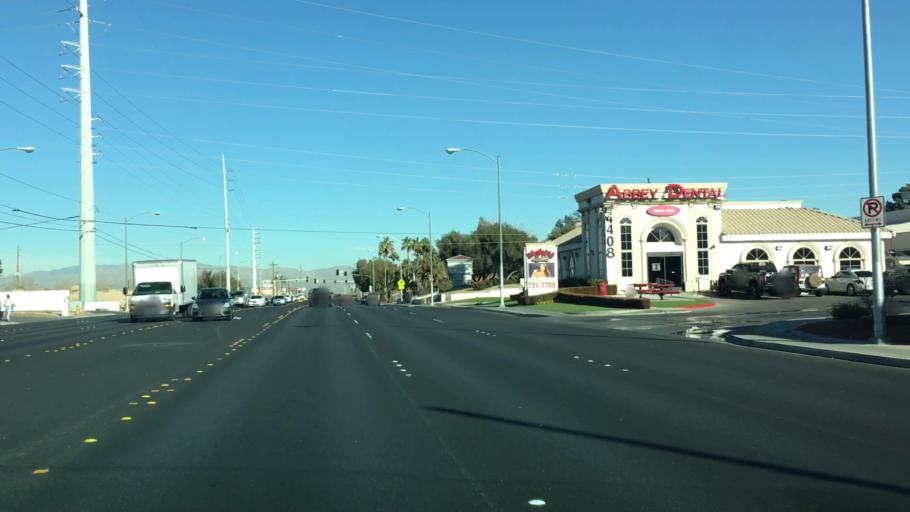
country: US
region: Nevada
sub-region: Clark County
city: Winchester
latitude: 36.1084
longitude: -115.1191
